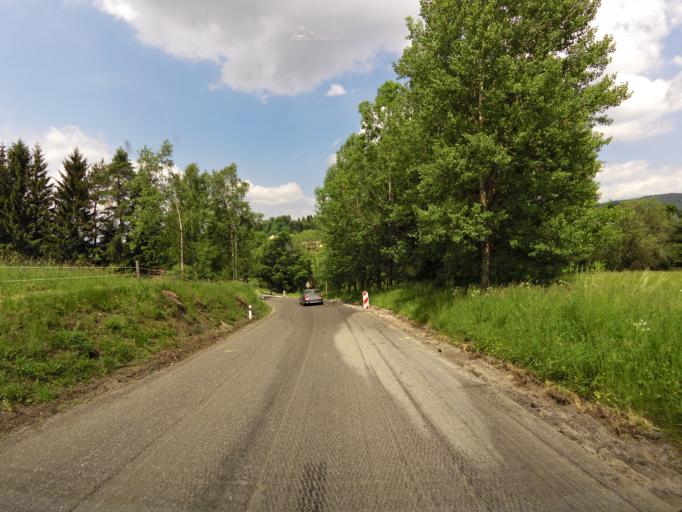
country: CZ
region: Jihocesky
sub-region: Okres Cesky Krumlov
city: Horni Plana
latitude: 48.7890
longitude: 13.9999
